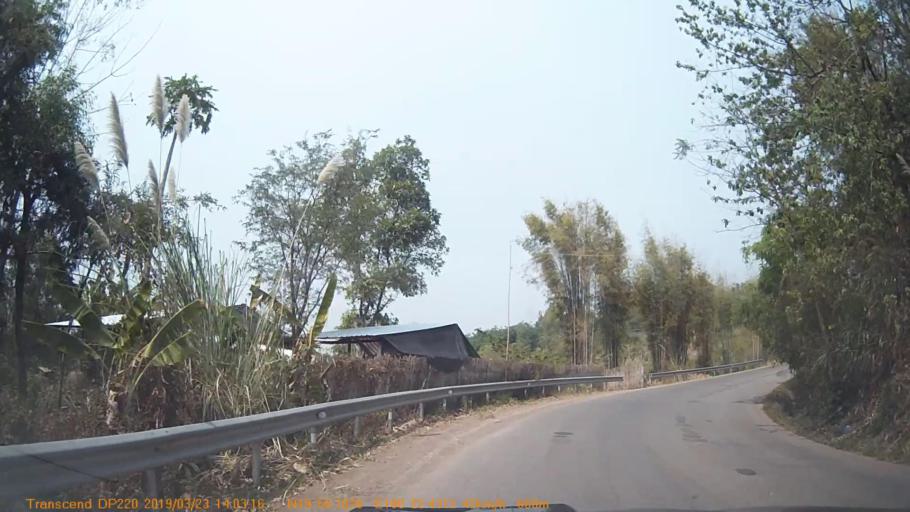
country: TH
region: Chiang Rai
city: Khun Tan
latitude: 19.8366
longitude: 100.3739
